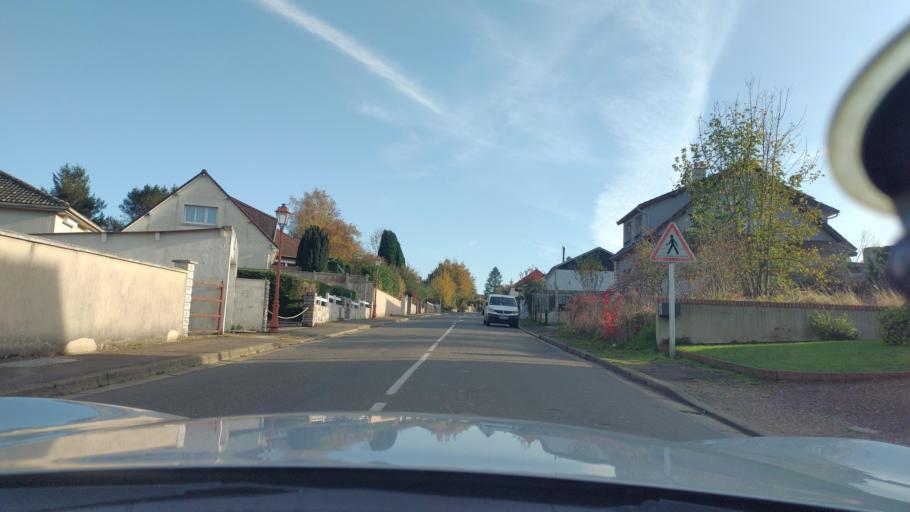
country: FR
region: Picardie
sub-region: Departement de la Somme
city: Fressenneville
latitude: 50.0702
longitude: 1.5667
